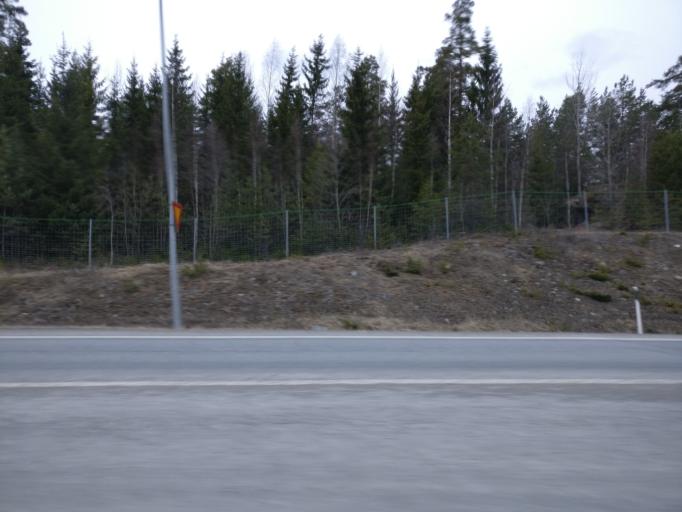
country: FI
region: Pirkanmaa
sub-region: Tampere
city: Lempaeaelae
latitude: 61.2906
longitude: 23.8129
